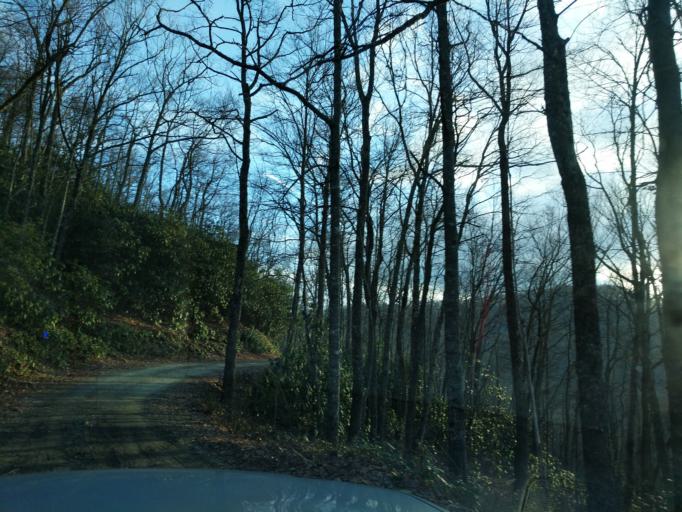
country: US
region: North Carolina
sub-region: Haywood County
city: Cove Creek
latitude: 35.7321
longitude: -83.0543
